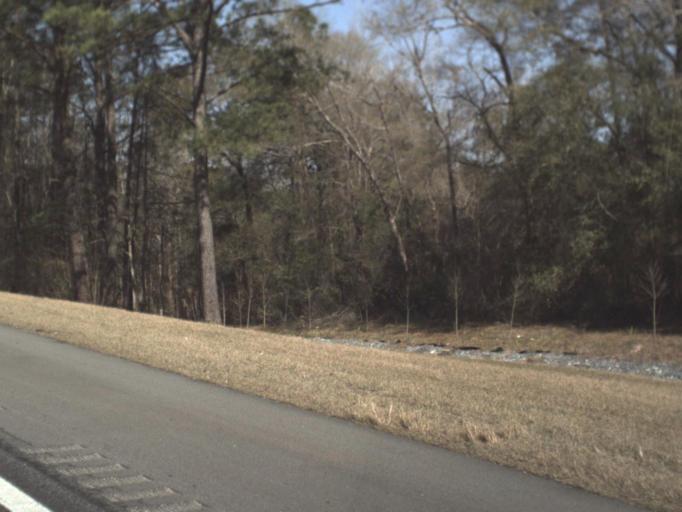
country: US
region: Florida
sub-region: Gadsden County
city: Chattahoochee
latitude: 30.6298
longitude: -84.8574
